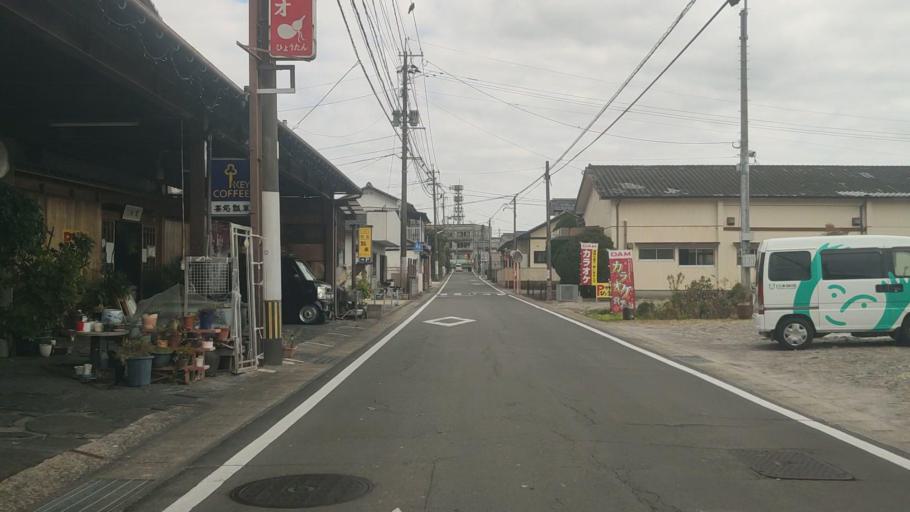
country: JP
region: Nagasaki
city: Shimabara
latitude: 32.7634
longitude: 130.3660
